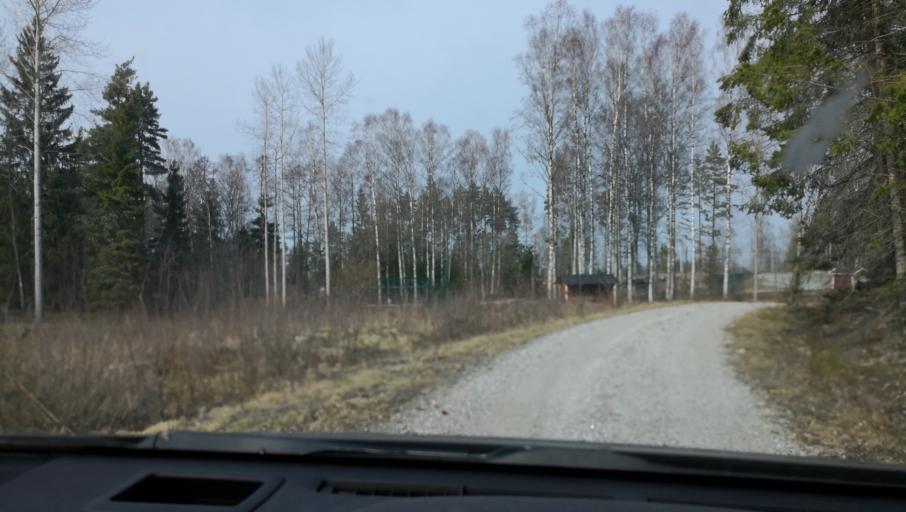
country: SE
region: OErebro
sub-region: Lindesbergs Kommun
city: Frovi
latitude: 59.3891
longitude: 15.4025
